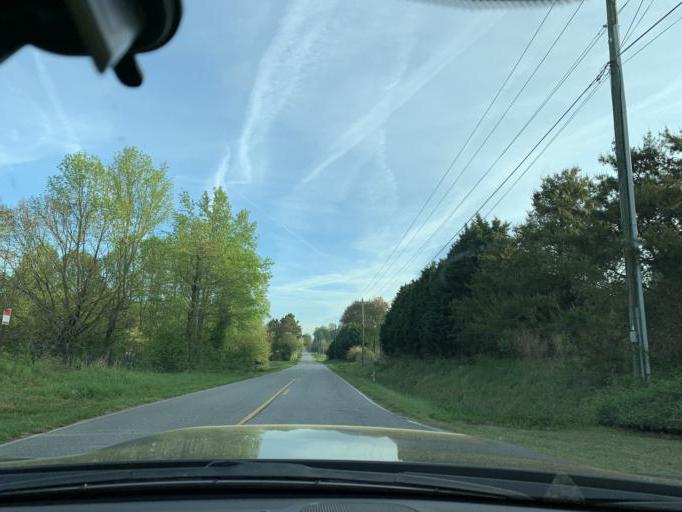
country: US
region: Georgia
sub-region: Forsyth County
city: Cumming
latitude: 34.2511
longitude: -84.1570
